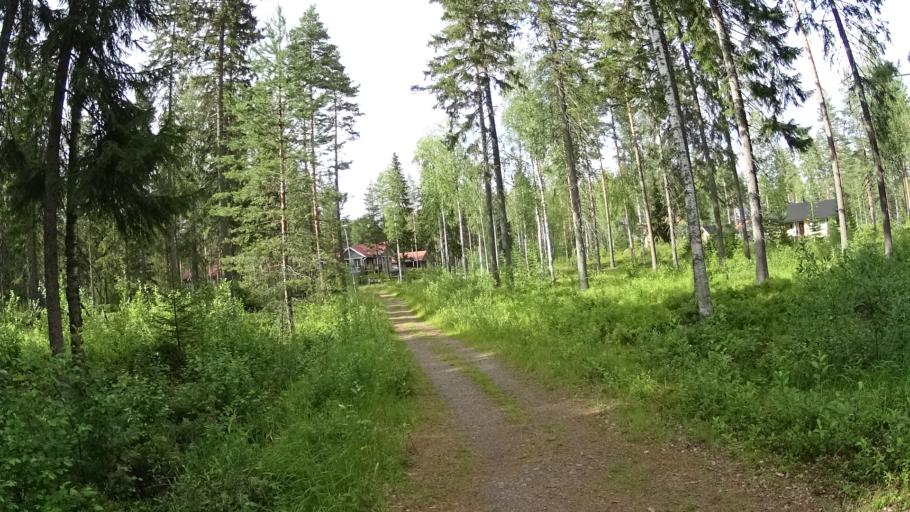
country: FI
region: Southern Ostrobothnia
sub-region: Kuusiokunnat
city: AEhtaeri
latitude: 62.5286
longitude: 24.1936
